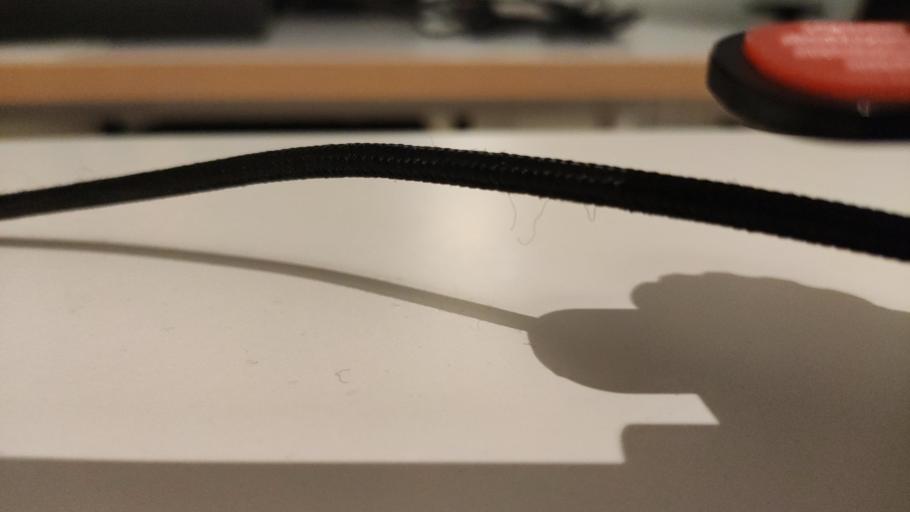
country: RU
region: Moskovskaya
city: Rogachevo
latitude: 56.4315
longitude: 37.1808
